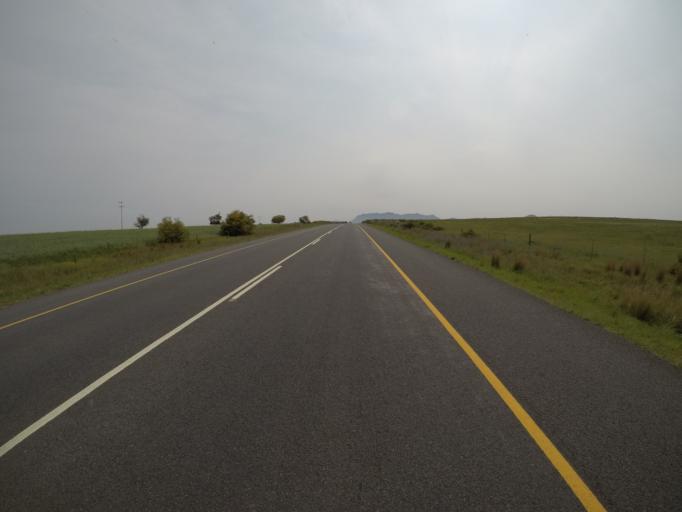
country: ZA
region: Western Cape
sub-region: West Coast District Municipality
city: Malmesbury
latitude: -33.5216
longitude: 18.8466
